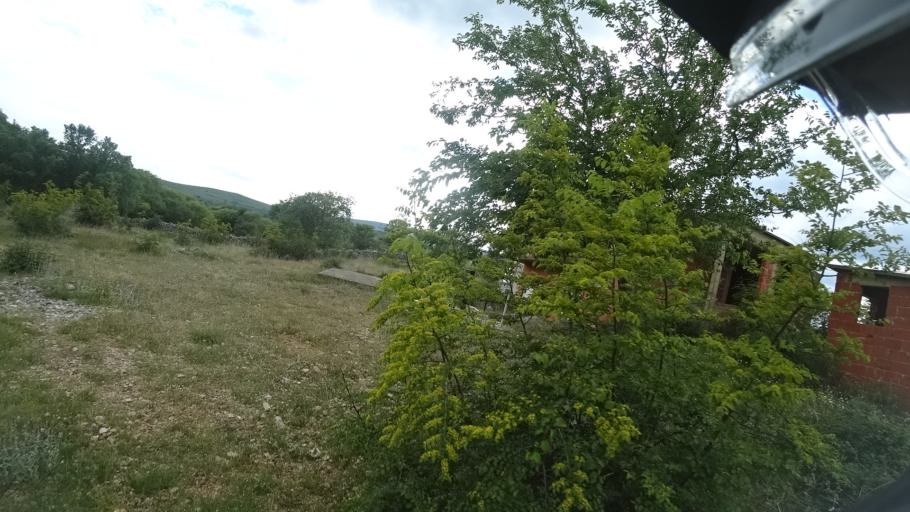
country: HR
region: Sibensko-Kniniska
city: Kistanje
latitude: 44.1136
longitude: 15.9364
